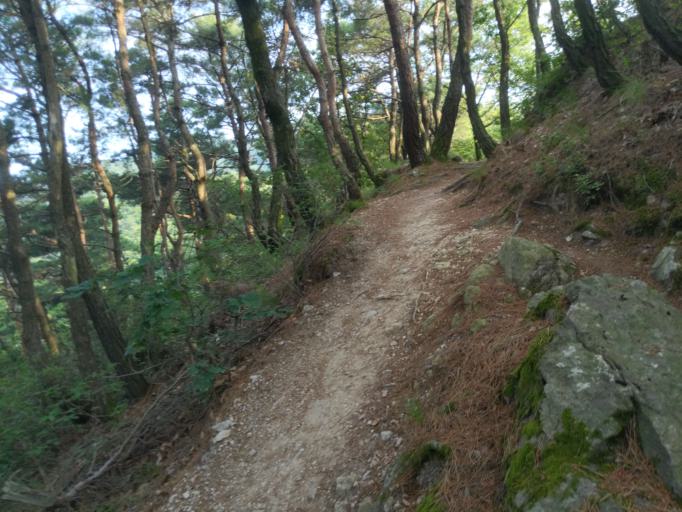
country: KR
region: Daegu
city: Hwawon
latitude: 35.7847
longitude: 128.5461
